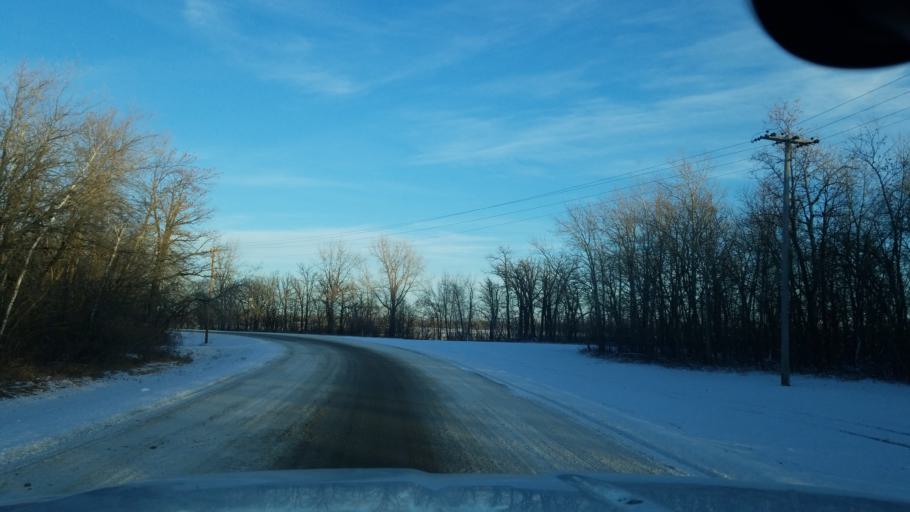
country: CA
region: Manitoba
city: Portage la Prairie
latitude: 49.9455
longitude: -98.3426
